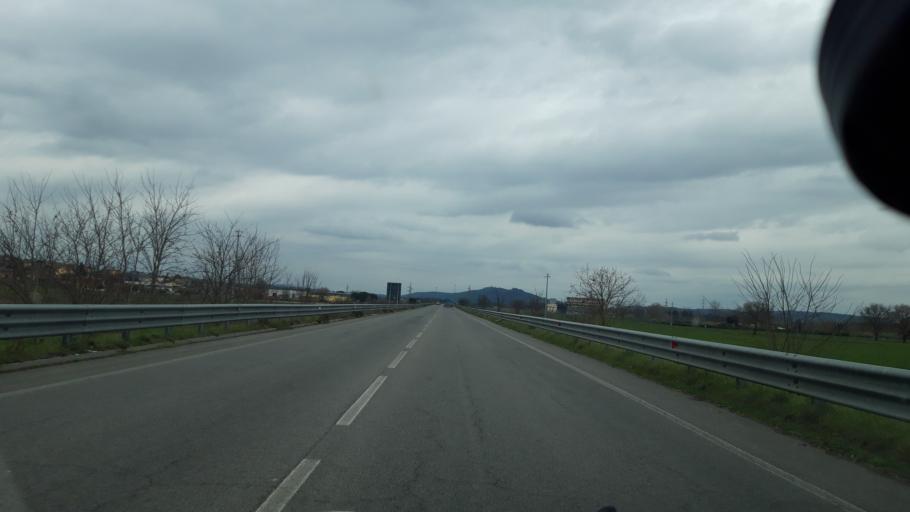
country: IT
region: Umbria
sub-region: Provincia di Perugia
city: Tavernelle
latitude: 43.0020
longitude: 12.1656
